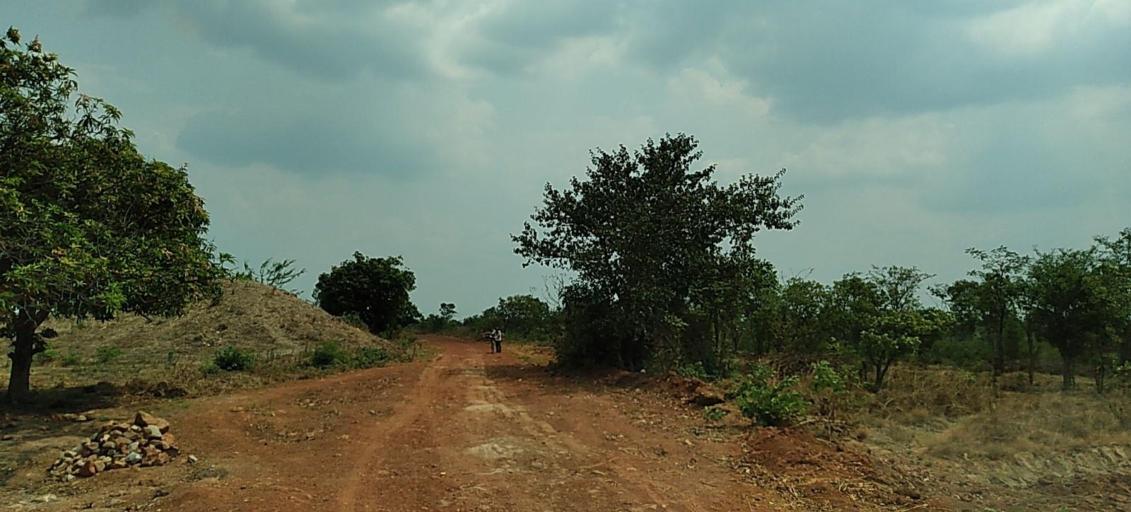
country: ZM
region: Copperbelt
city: Kalulushi
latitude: -12.8772
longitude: 28.0748
